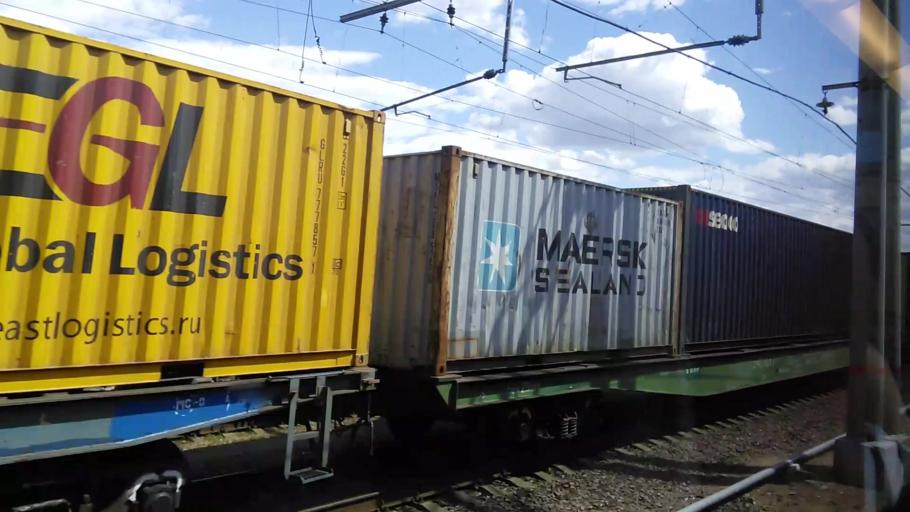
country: RU
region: Moscow
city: Mar'ina Roshcha
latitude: 55.8021
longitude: 37.5883
